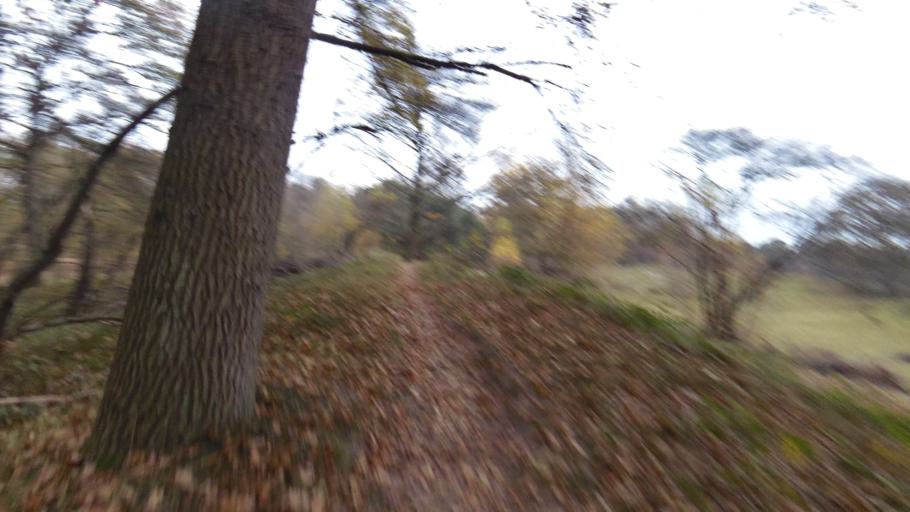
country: NL
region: North Holland
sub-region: Gemeente Laren
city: Laren
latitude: 52.2259
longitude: 5.2179
